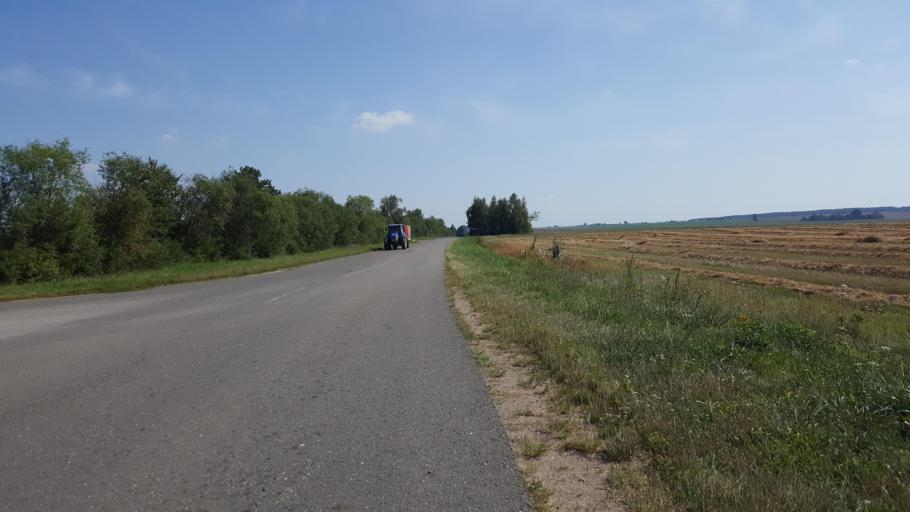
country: BY
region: Brest
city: Kamyanyets
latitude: 52.4757
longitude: 23.7056
